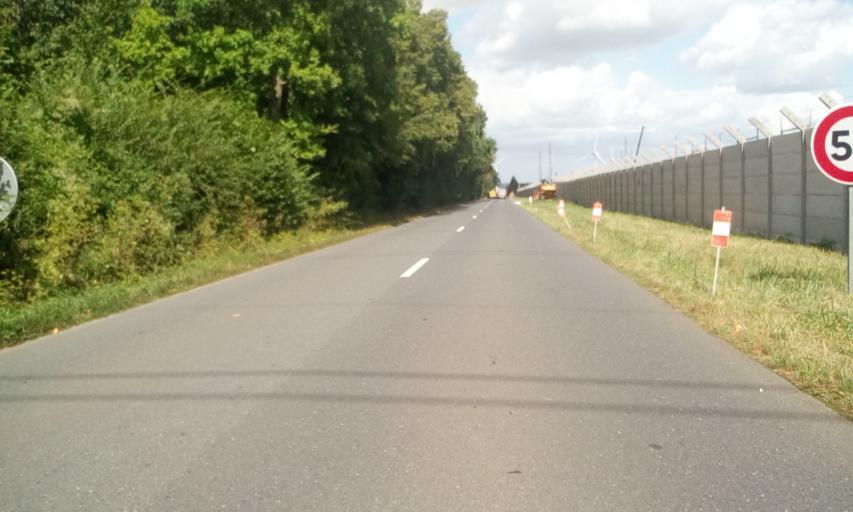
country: FR
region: Lower Normandy
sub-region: Departement du Calvados
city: Bourguebus
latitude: 49.1080
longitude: -0.2661
